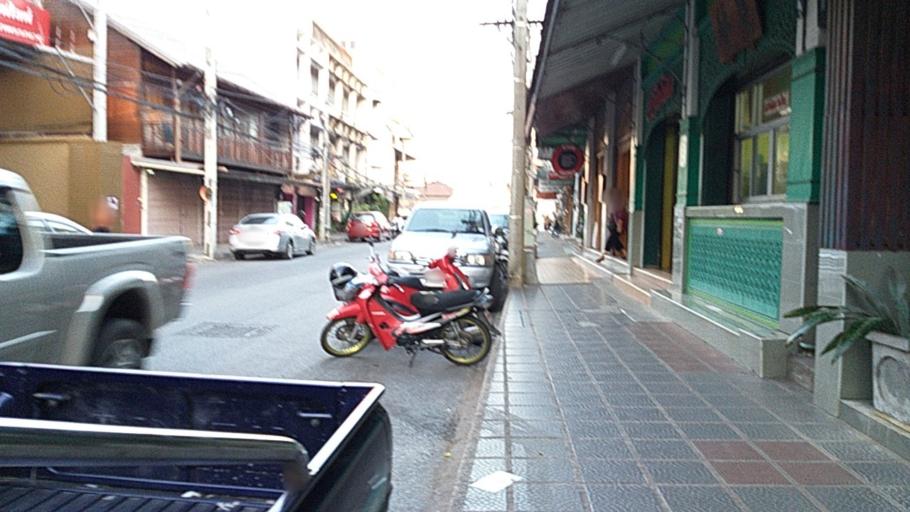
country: TH
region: Nakhon Ratchasima
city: Nakhon Ratchasima
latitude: 14.9750
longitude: 102.0971
